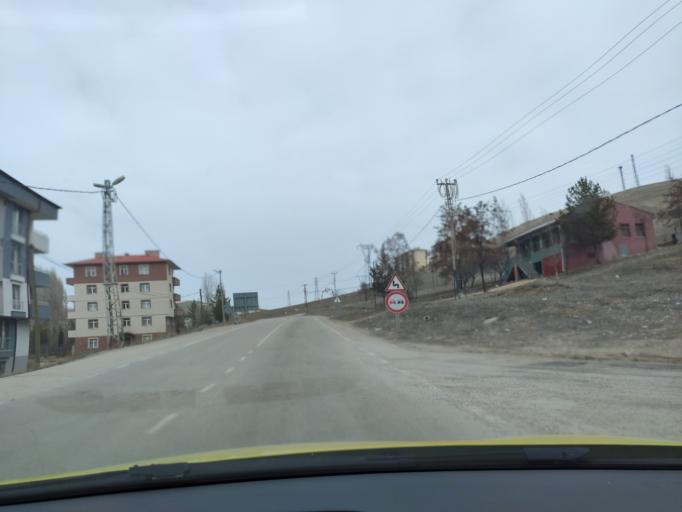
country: TR
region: Bayburt
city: Bayburt
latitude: 40.2620
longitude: 40.2145
